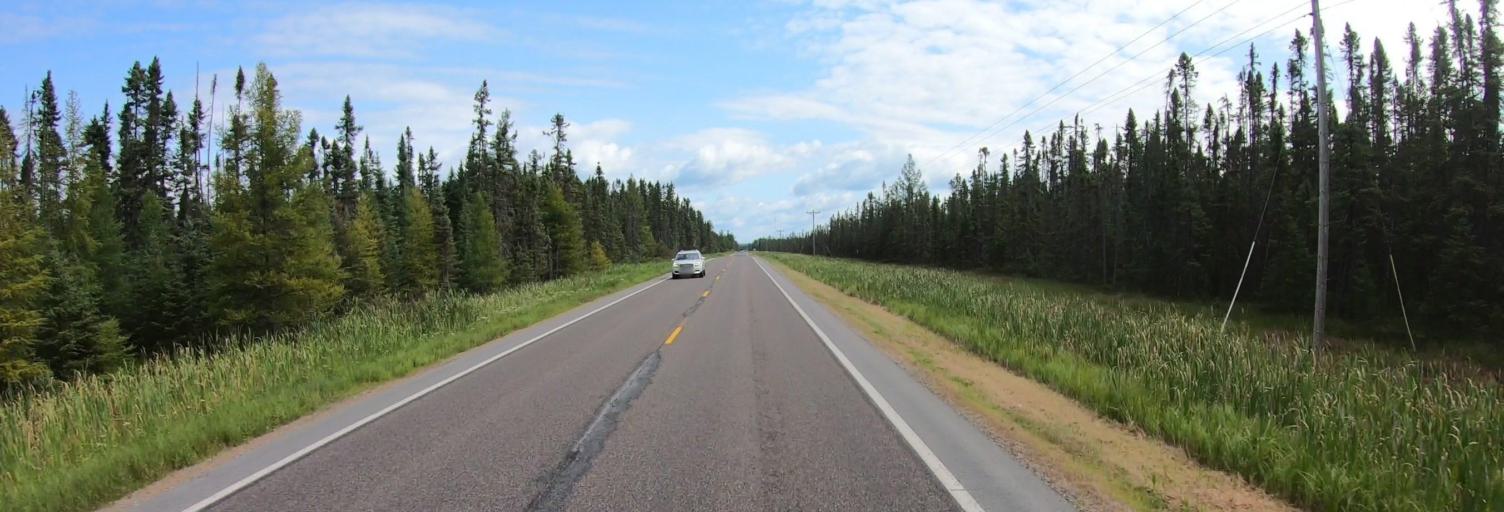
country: US
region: Minnesota
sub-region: Saint Louis County
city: Mountain Iron
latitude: 47.8727
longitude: -92.6825
